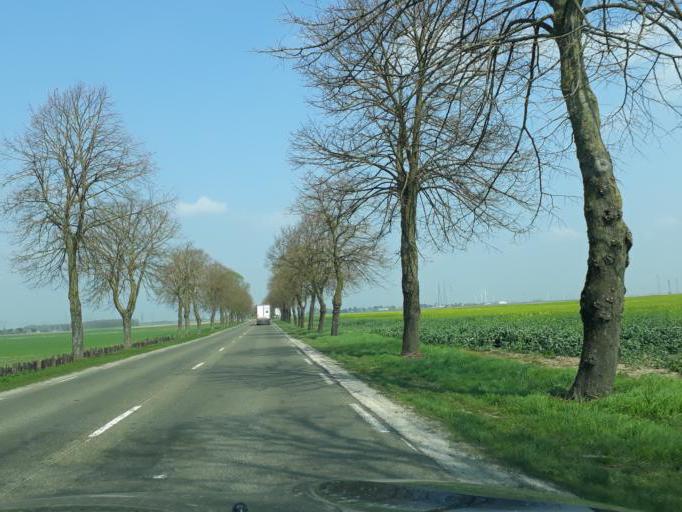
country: FR
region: Centre
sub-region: Departement du Loiret
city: Artenay
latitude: 48.0918
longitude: 1.8654
